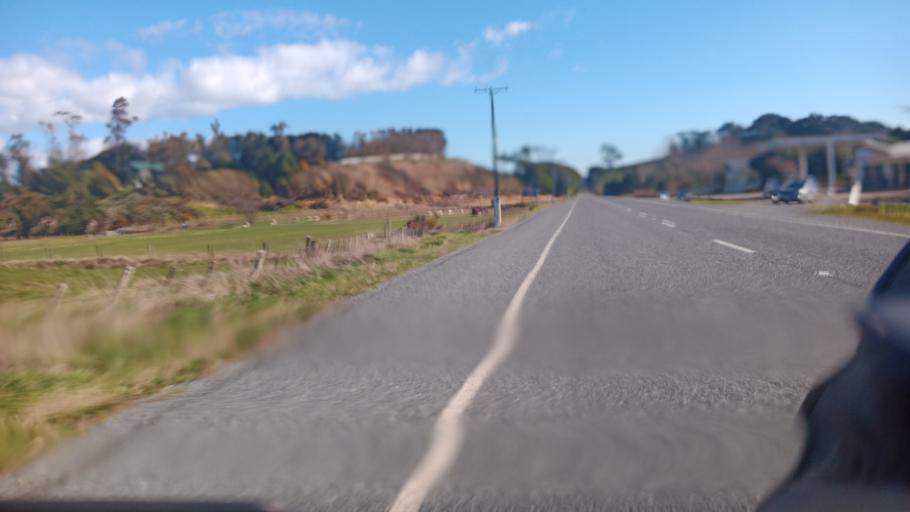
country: NZ
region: Bay of Plenty
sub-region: Opotiki District
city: Opotiki
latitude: -37.9887
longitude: 177.3534
